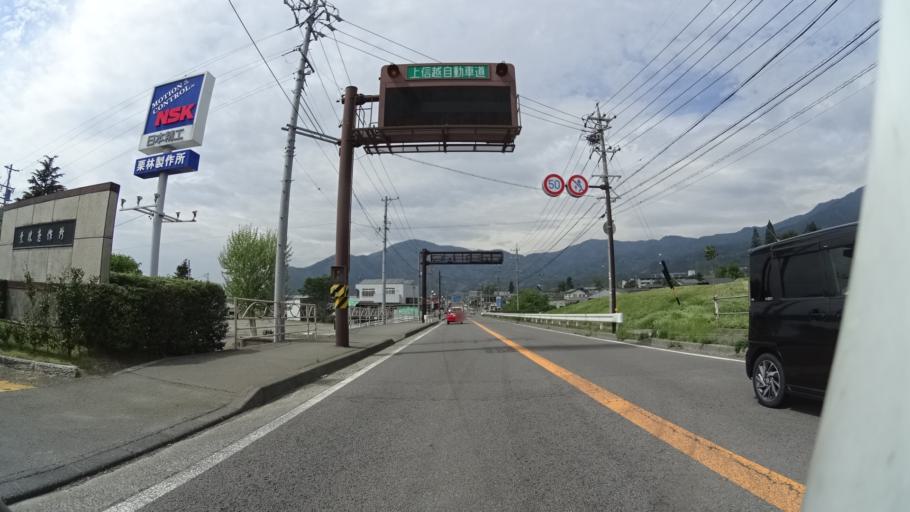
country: JP
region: Nagano
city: Ueda
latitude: 36.4425
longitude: 138.1905
